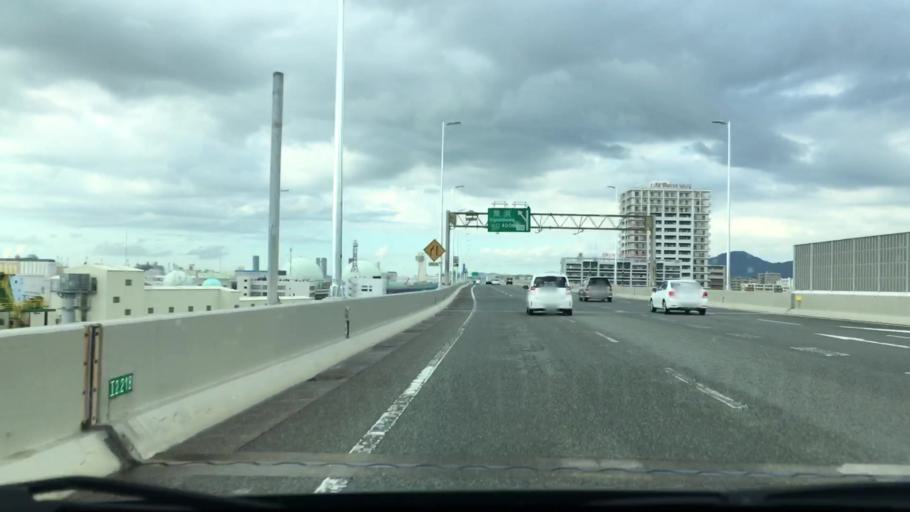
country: JP
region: Fukuoka
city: Fukuoka-shi
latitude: 33.6106
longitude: 130.4090
